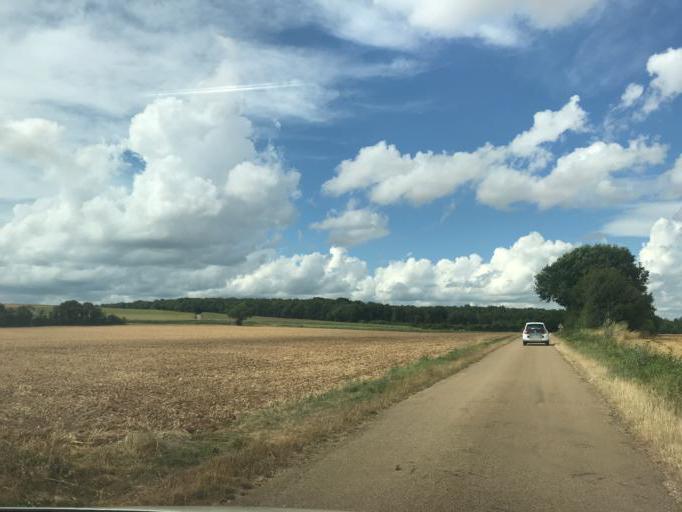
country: FR
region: Bourgogne
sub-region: Departement de l'Yonne
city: Fontenailles
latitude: 47.5842
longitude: 3.3454
